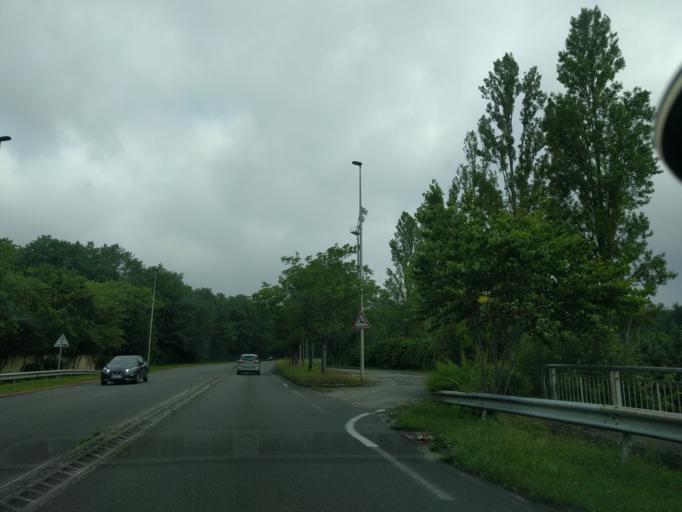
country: FR
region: Poitou-Charentes
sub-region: Departement de la Charente
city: Angouleme
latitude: 45.6321
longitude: 0.1446
